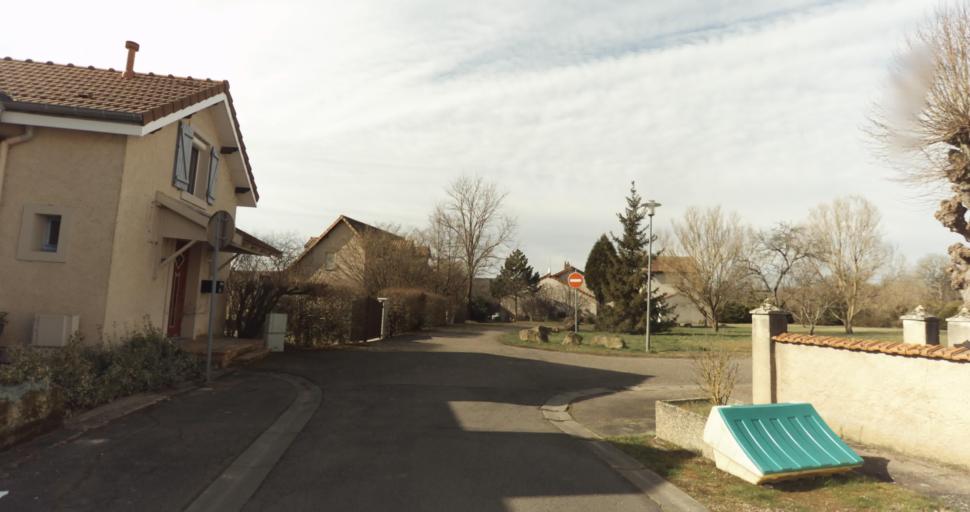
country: FR
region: Lorraine
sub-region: Departement de Meurthe-et-Moselle
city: Jarny
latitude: 49.1507
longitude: 5.8605
